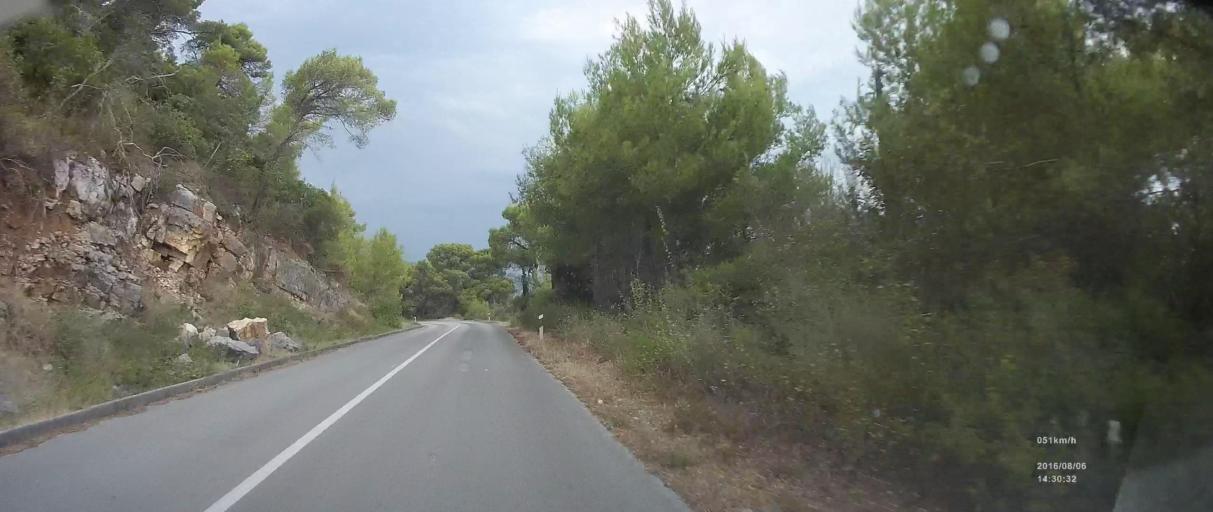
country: HR
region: Dubrovacko-Neretvanska
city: Ston
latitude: 42.7111
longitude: 17.7273
